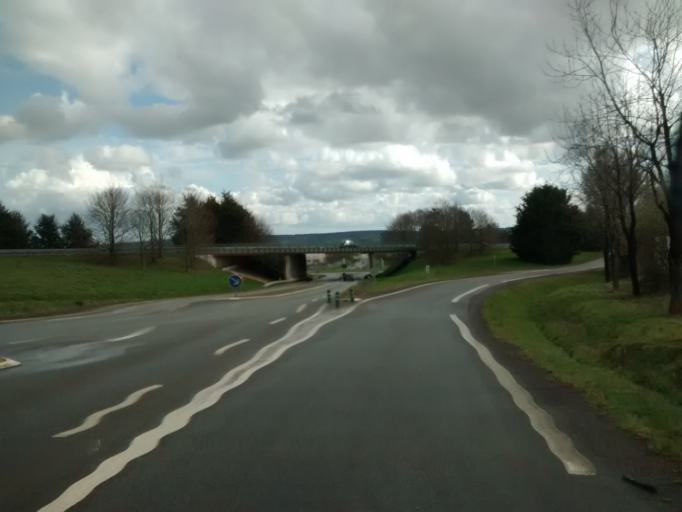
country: FR
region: Brittany
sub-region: Departement du Morbihan
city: Malestroit
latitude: 47.8527
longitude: -2.4206
